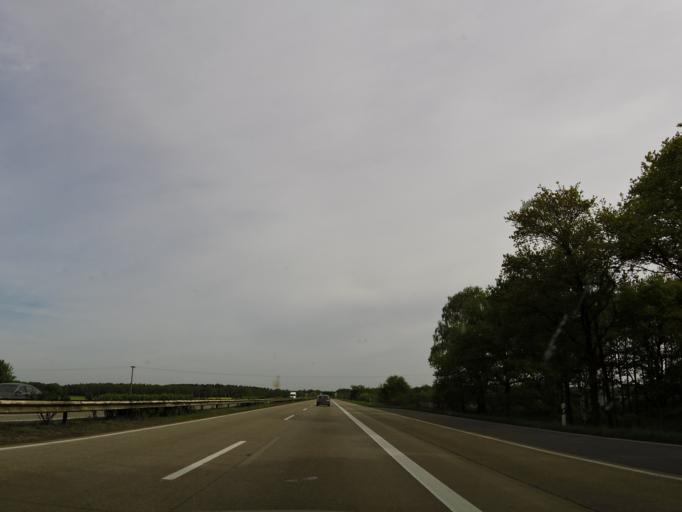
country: DE
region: Lower Saxony
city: Bad Fallingbostel
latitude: 52.8286
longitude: 9.6851
